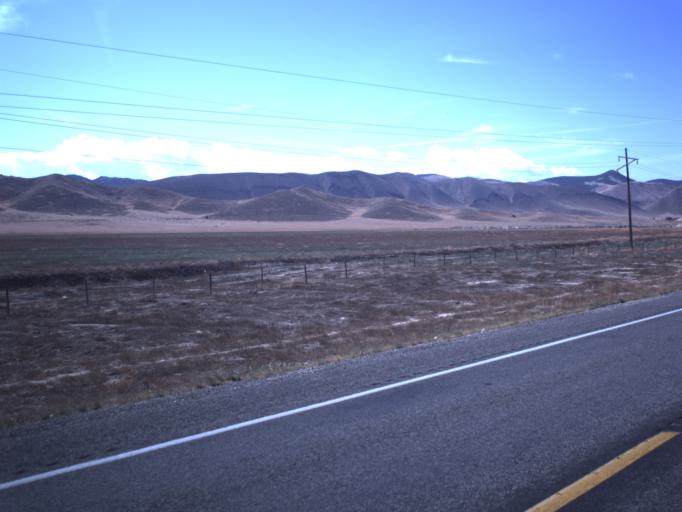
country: US
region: Utah
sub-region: Sevier County
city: Salina
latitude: 39.0254
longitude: -111.8314
